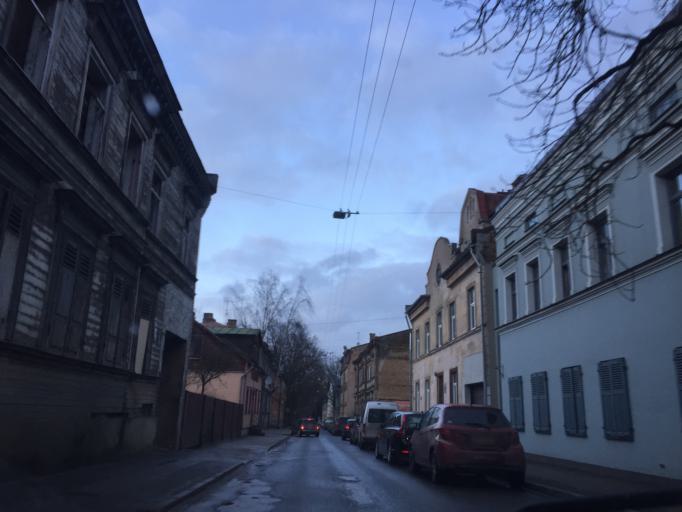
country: LV
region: Riga
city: Riga
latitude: 56.9394
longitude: 24.0787
